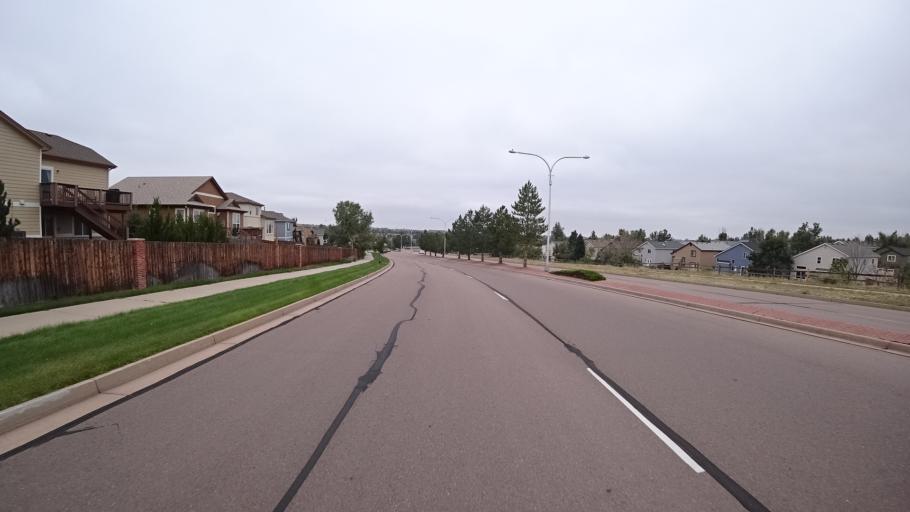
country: US
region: Colorado
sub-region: El Paso County
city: Cimarron Hills
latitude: 38.9083
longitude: -104.7097
